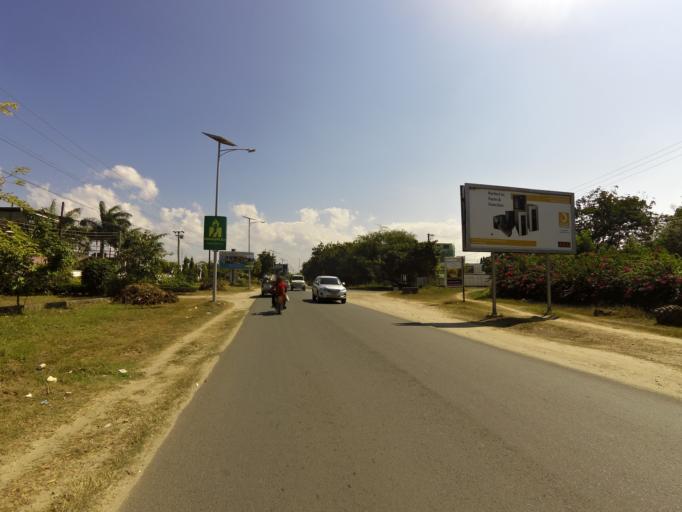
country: TZ
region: Dar es Salaam
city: Magomeni
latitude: -6.7579
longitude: 39.2812
